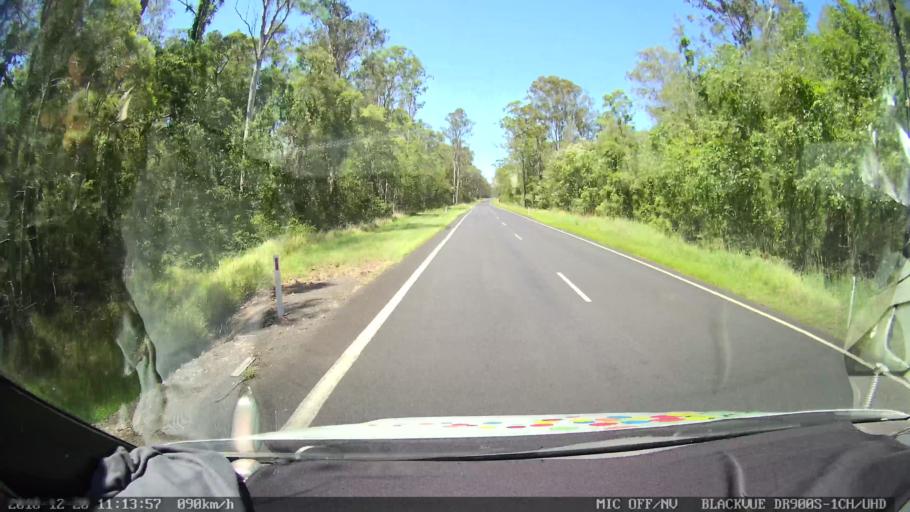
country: AU
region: New South Wales
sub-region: Richmond Valley
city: Casino
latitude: -28.9946
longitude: 153.0110
